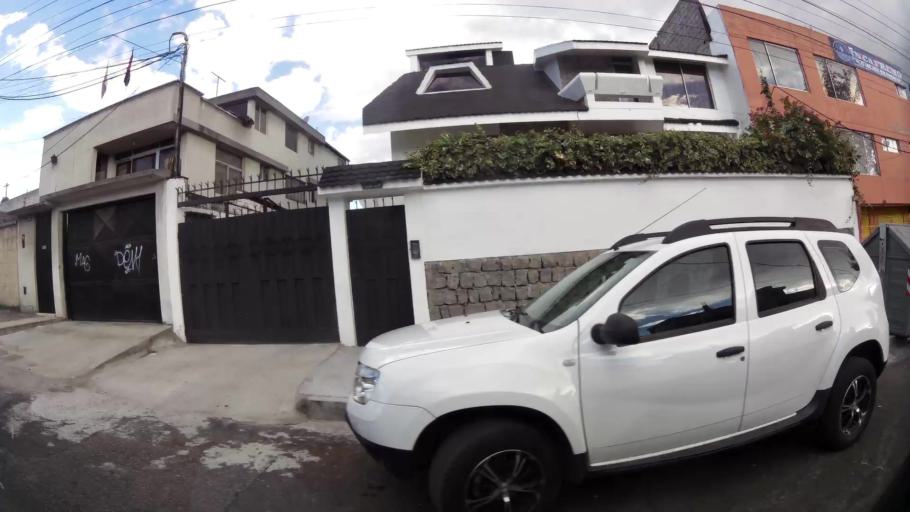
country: EC
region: Pichincha
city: Quito
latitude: -0.1308
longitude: -78.4869
